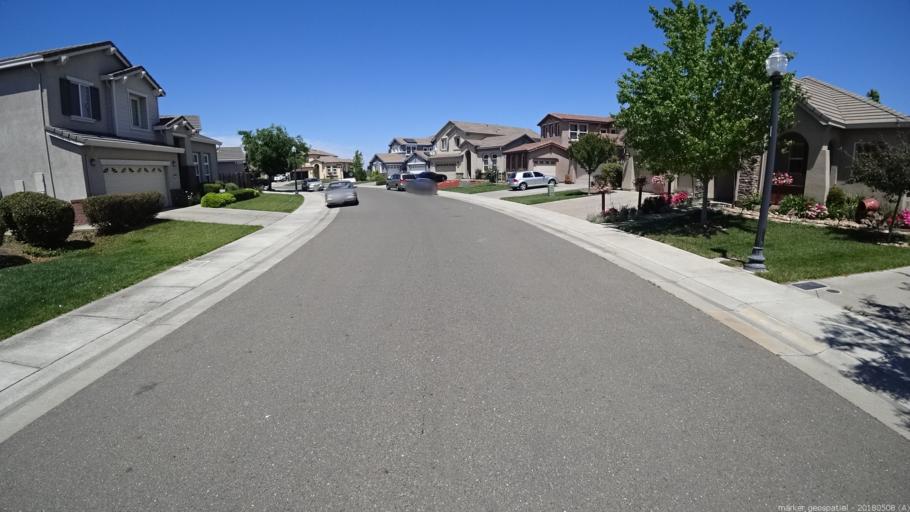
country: US
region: California
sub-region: Sacramento County
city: Elverta
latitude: 38.6837
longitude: -121.5280
